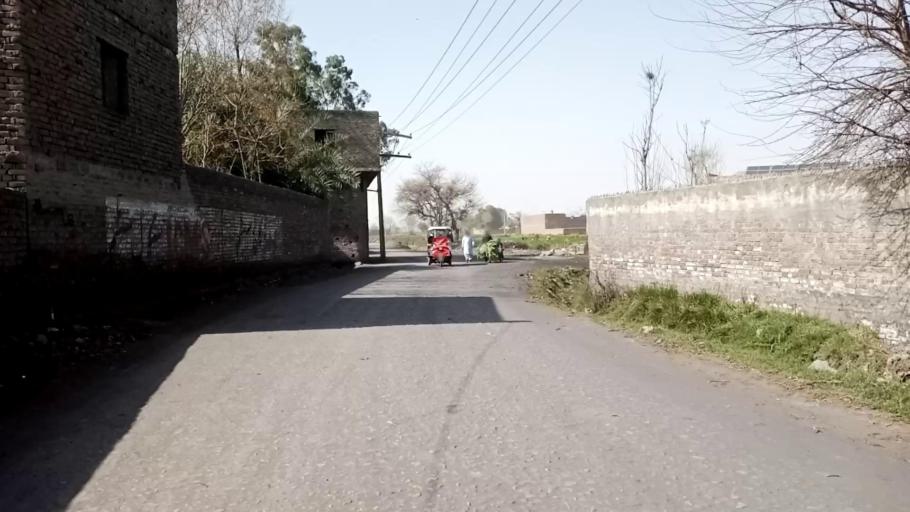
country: PK
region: Khyber Pakhtunkhwa
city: Peshawar
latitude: 34.0178
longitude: 71.6433
